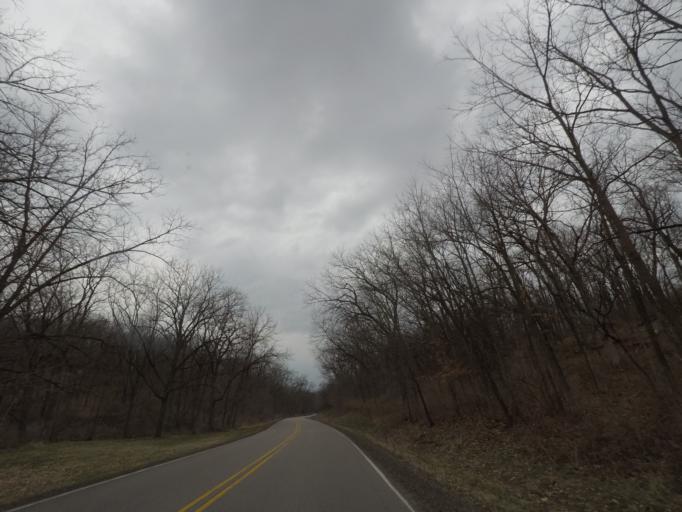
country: US
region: Wisconsin
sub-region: Dane County
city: Cross Plains
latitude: 43.1073
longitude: -89.5838
